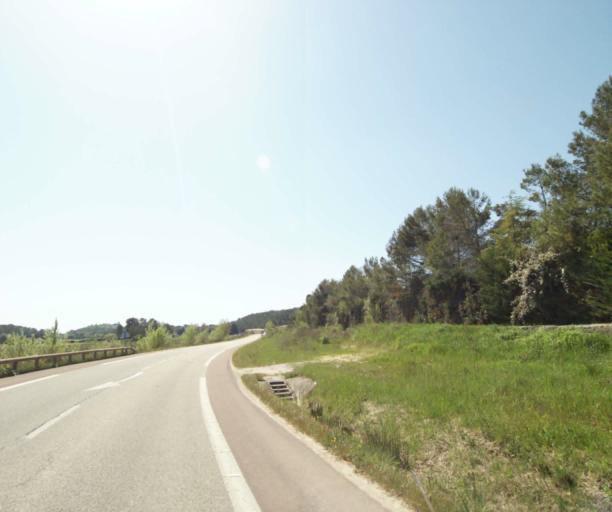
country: FR
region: Languedoc-Roussillon
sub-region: Departement de l'Herault
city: Montferrier-sur-Lez
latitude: 43.6810
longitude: 3.8569
